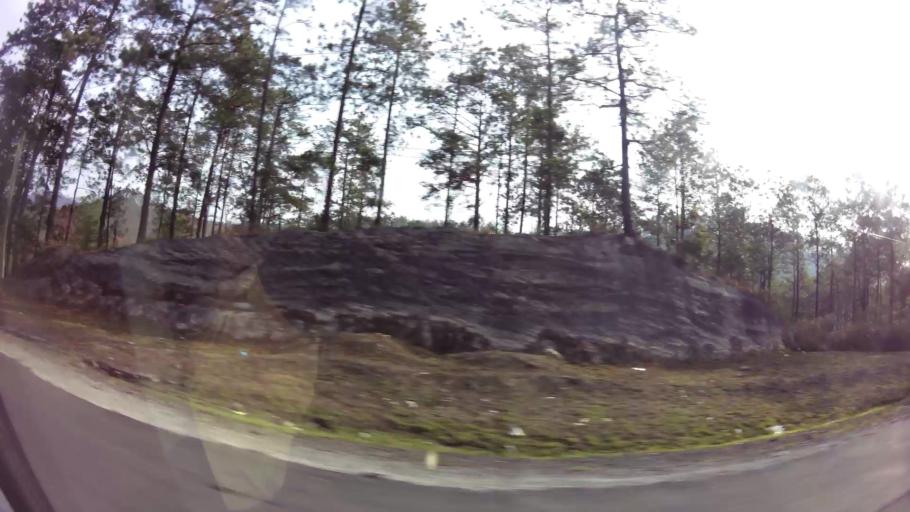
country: HN
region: Francisco Morazan
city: Zambrano
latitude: 14.2855
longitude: -87.4531
